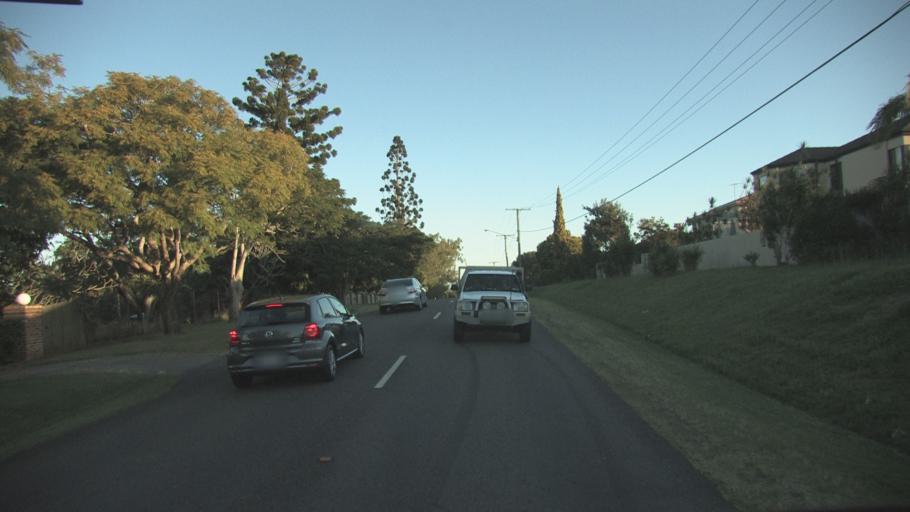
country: AU
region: Queensland
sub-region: Logan
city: Rochedale South
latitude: -27.6055
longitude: 153.1036
